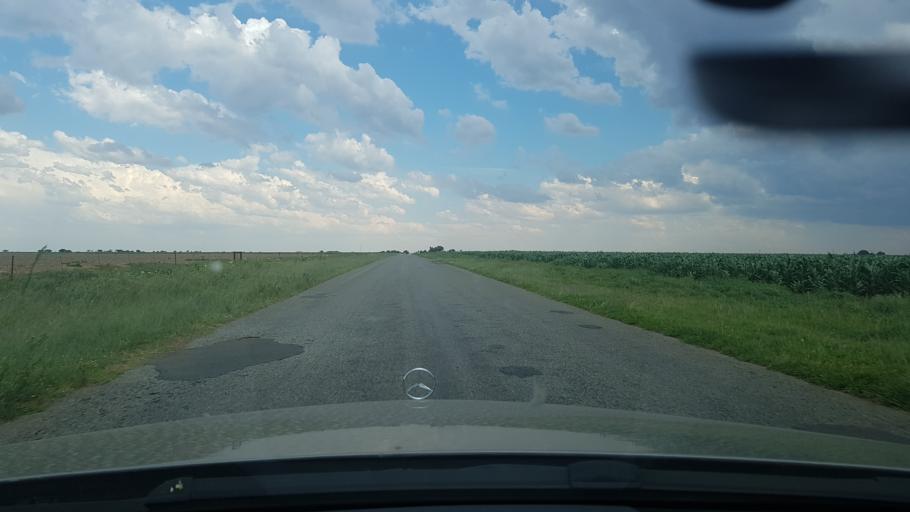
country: ZA
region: Orange Free State
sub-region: Lejweleputswa District Municipality
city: Hoopstad
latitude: -27.9078
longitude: 25.6788
